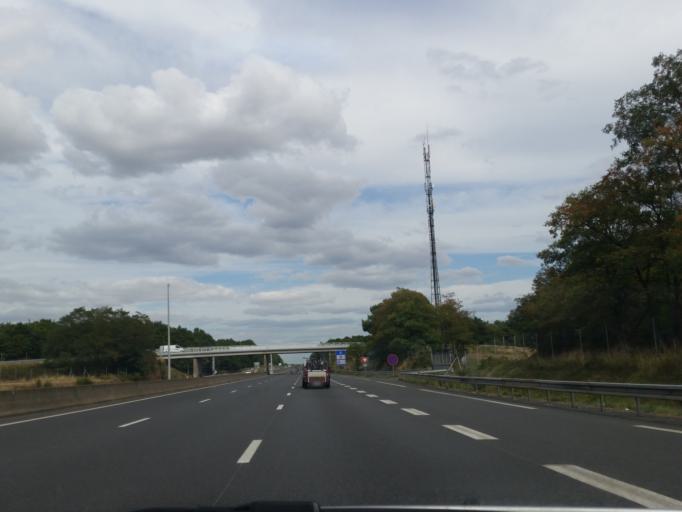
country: FR
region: Centre
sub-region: Departement d'Indre-et-Loire
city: Monnaie
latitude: 47.4912
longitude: 0.8235
